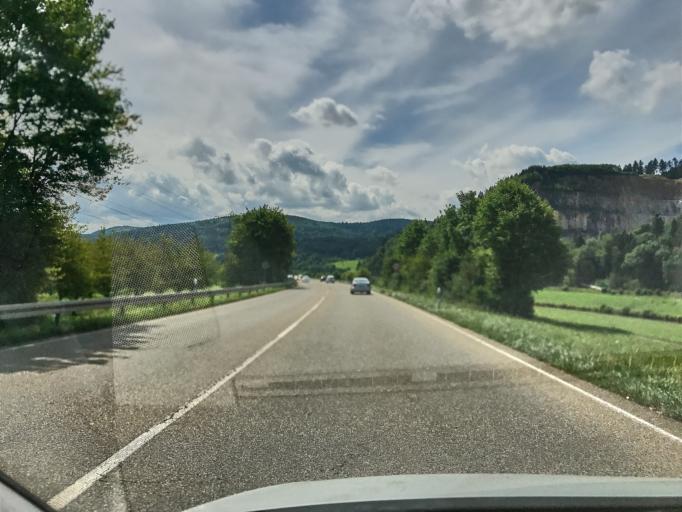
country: DE
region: Baden-Wuerttemberg
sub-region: Freiburg Region
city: Steinach
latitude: 48.2984
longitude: 8.0624
